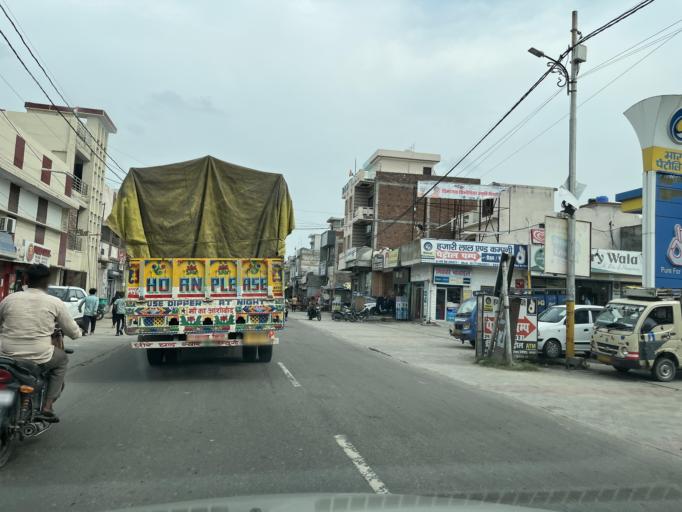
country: IN
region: Uttar Pradesh
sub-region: Rampur
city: Bilaspur
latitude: 29.0424
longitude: 79.2480
